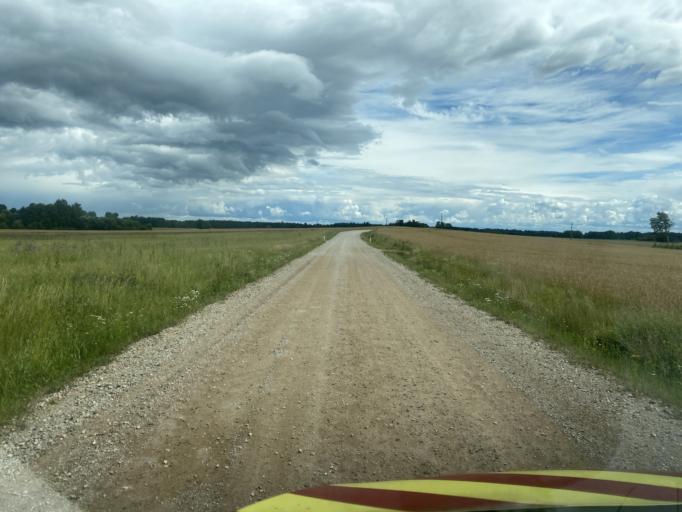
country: EE
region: Valgamaa
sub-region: Torva linn
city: Torva
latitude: 57.9530
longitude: 25.9543
